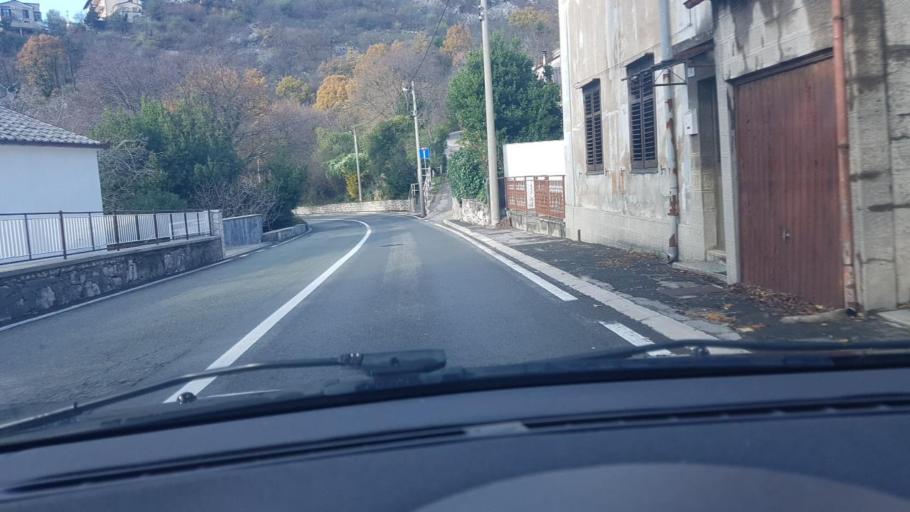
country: HR
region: Primorsko-Goranska
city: Cavle
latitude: 45.3524
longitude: 14.4659
